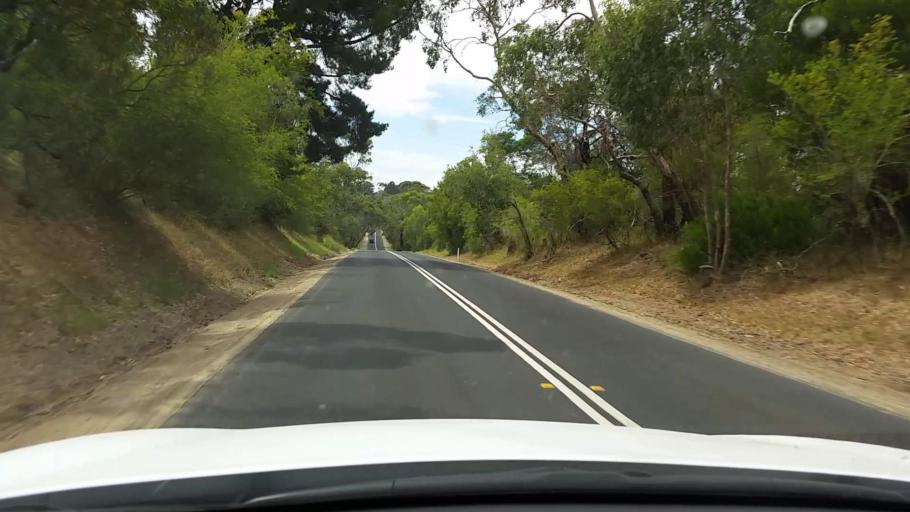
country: AU
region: Victoria
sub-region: Mornington Peninsula
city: Mount Martha
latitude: -38.2901
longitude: 145.0563
